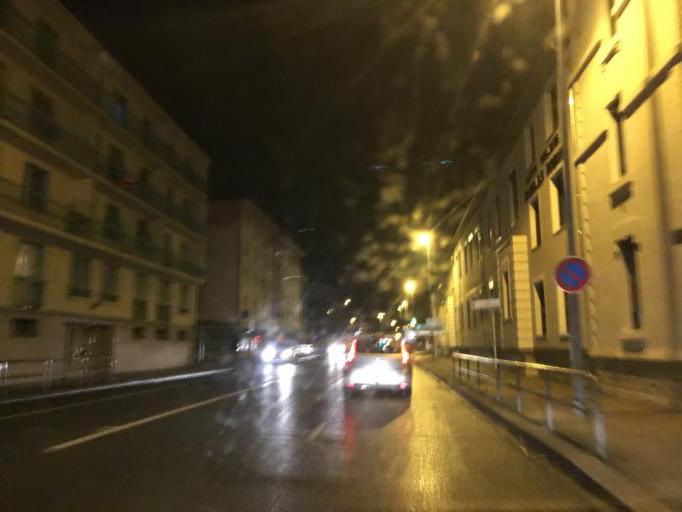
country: FR
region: Rhone-Alpes
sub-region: Departement de l'Ain
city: Bourg-en-Bresse
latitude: 46.2060
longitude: 5.2348
